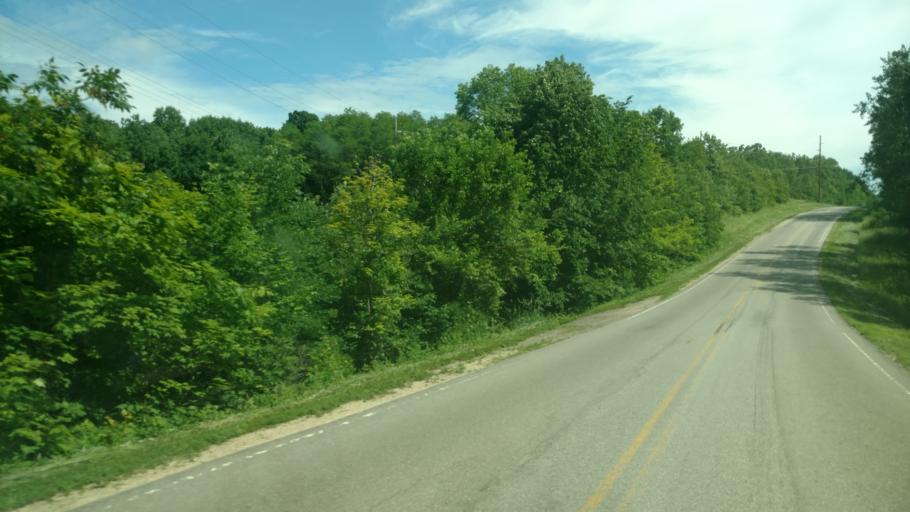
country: US
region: Wisconsin
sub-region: Vernon County
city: Hillsboro
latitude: 43.6725
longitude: -90.4577
